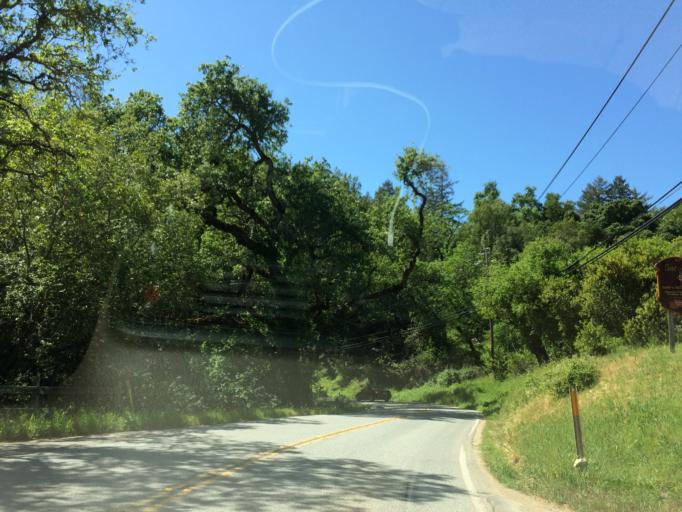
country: US
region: California
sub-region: Santa Clara County
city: Lexington Hills
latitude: 37.1858
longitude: -122.0020
